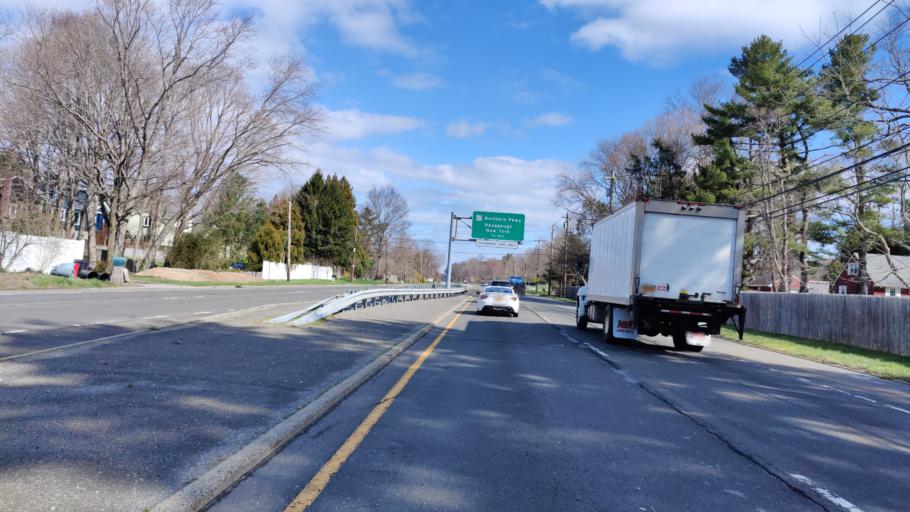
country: US
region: New York
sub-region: Suffolk County
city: Dix Hills
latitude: 40.8127
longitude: -73.3422
